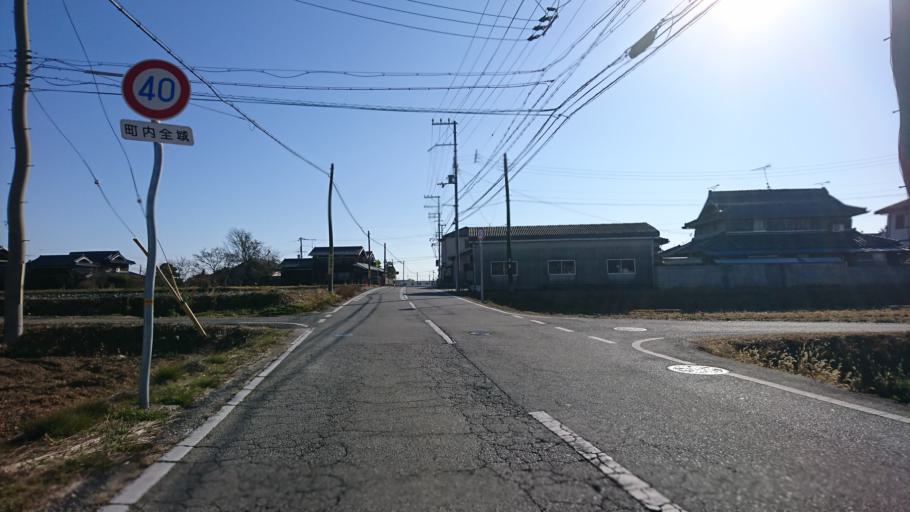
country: JP
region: Hyogo
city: Miki
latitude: 34.7503
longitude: 134.9276
